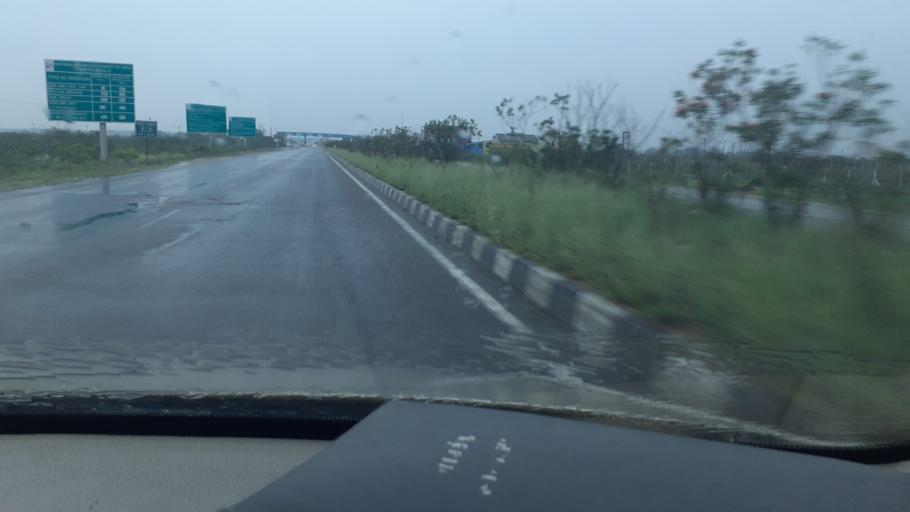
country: IN
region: Tamil Nadu
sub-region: Virudhunagar
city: Sattur
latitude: 9.3893
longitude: 77.9149
